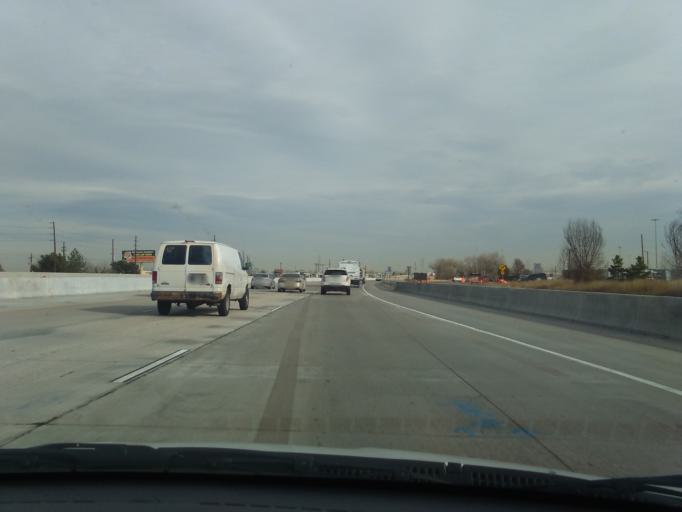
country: US
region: Colorado
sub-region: Adams County
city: Derby
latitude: 39.8749
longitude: -104.8971
